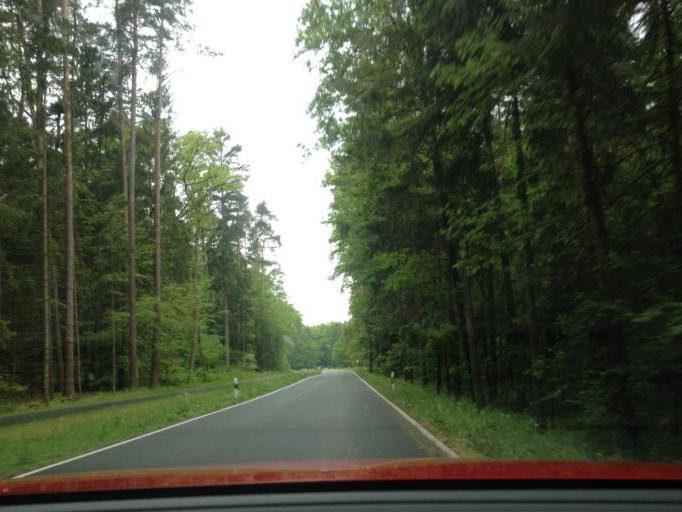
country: DE
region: Bavaria
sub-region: Regierungsbezirk Mittelfranken
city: Lauf an der Pegnitz
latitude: 49.4827
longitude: 11.2837
